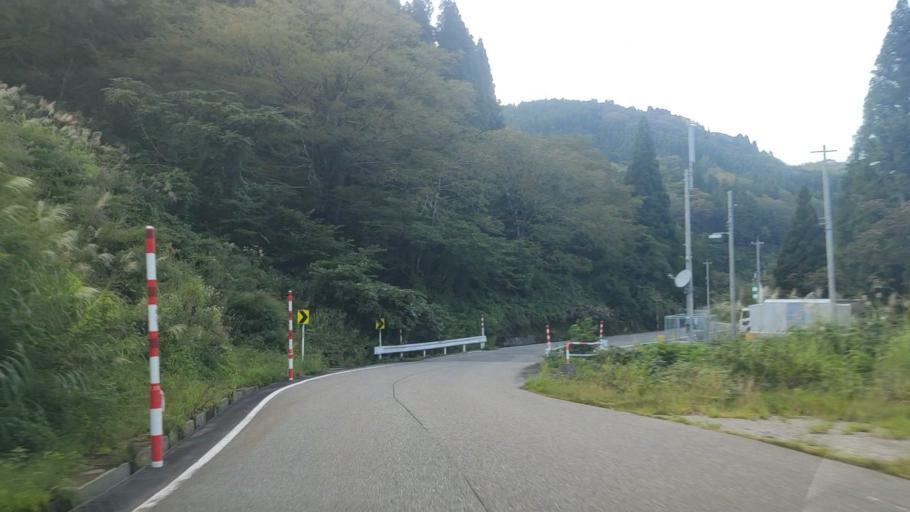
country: JP
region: Toyama
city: Yatsuomachi-higashikumisaka
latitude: 36.4910
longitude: 137.0637
